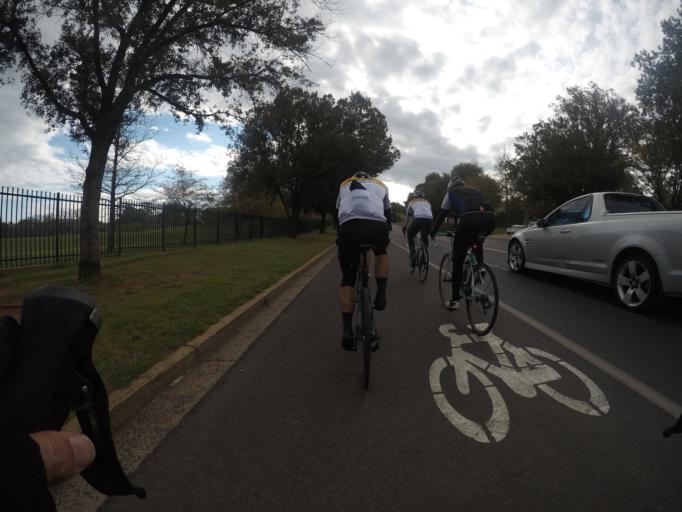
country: AU
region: New South Wales
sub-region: Orange Municipality
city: Orange
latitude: -33.2810
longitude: 149.0795
